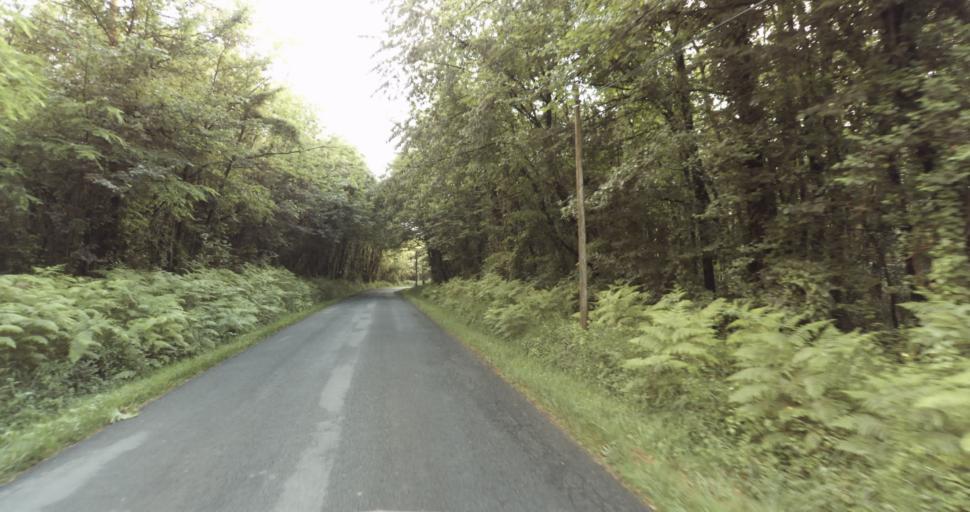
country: FR
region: Aquitaine
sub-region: Departement de la Dordogne
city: Le Bugue
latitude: 44.9346
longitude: 0.8181
